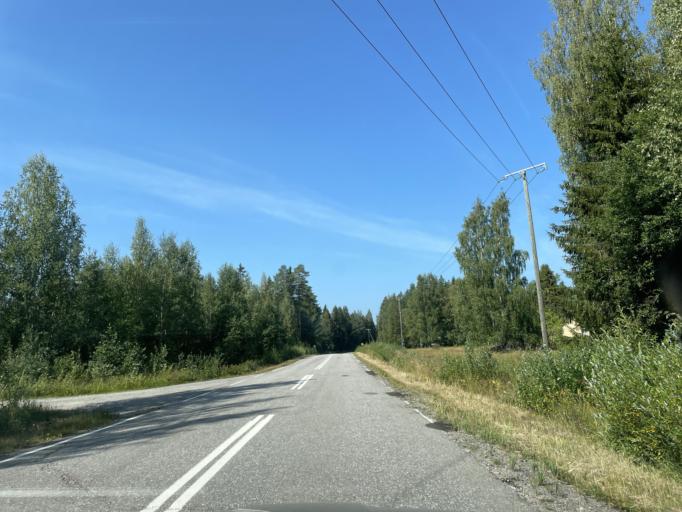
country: FI
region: Central Finland
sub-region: Saarijaervi-Viitasaari
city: Pihtipudas
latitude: 63.3548
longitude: 25.7644
